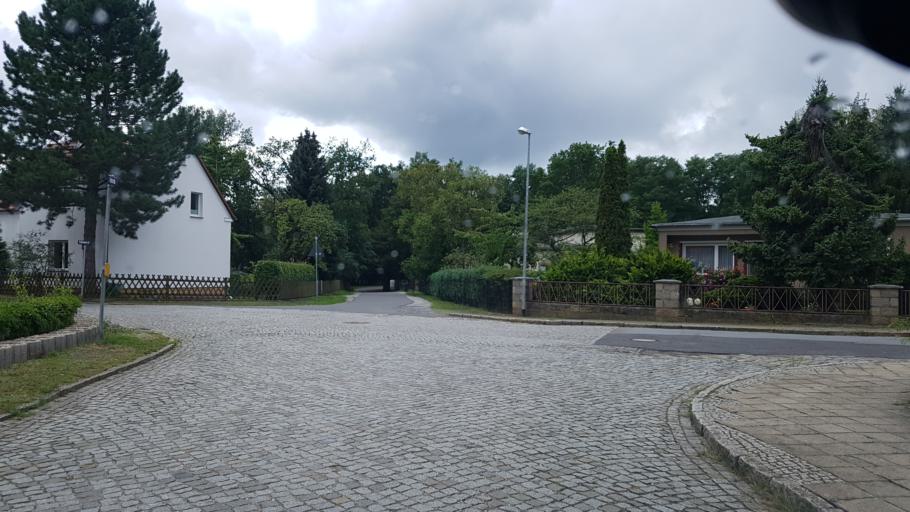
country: DE
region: Brandenburg
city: Tschernitz
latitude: 51.6115
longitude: 14.5981
